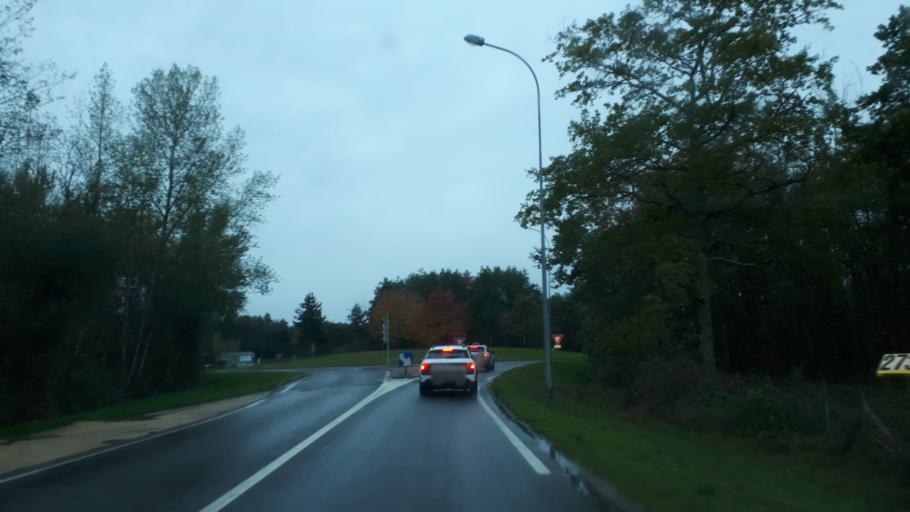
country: FR
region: Centre
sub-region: Departement du Loir-et-Cher
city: Gievres
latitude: 47.2978
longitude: 1.6723
